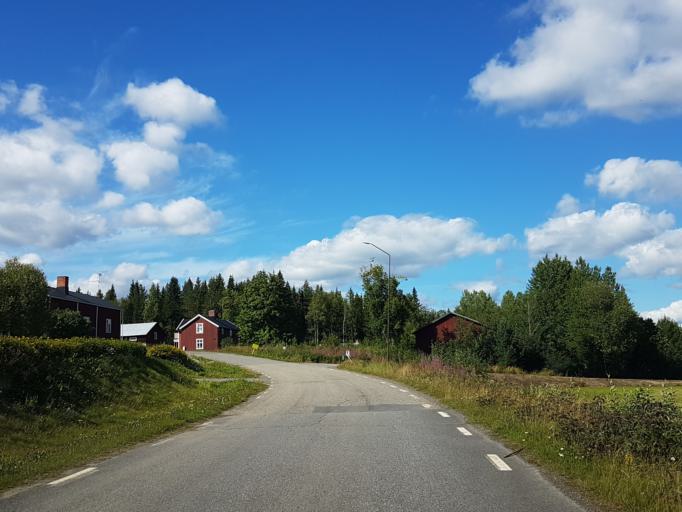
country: SE
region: Vaesterbotten
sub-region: Skelleftea Kommun
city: Burtraesk
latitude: 64.2709
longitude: 20.4907
